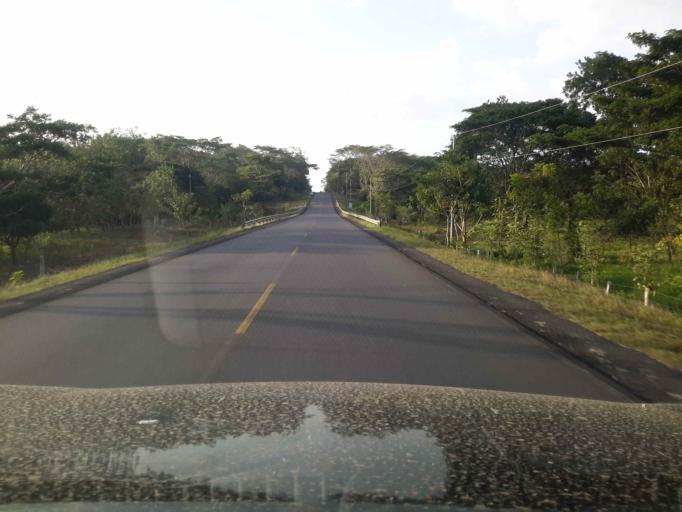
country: NI
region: Rio San Juan
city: San Miguelito
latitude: 11.3230
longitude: -84.7396
